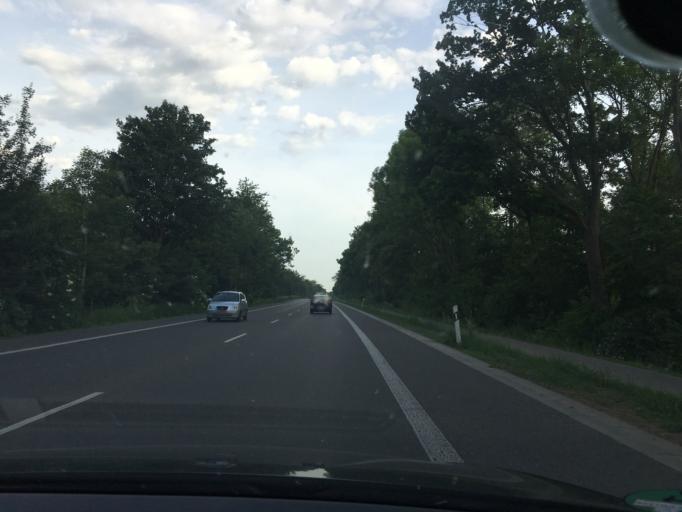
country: DE
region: North Rhine-Westphalia
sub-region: Regierungsbezirk Koln
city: Inden
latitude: 50.8838
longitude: 6.4077
